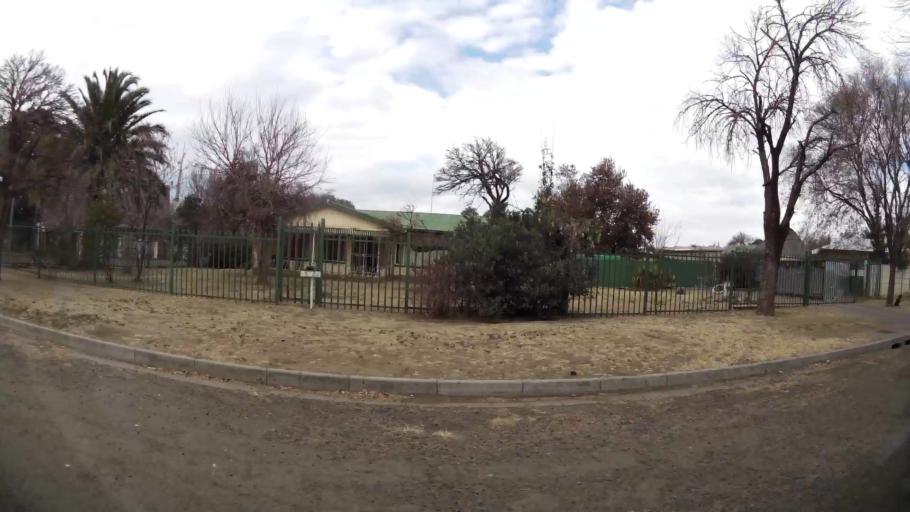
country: ZA
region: Orange Free State
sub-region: Fezile Dabi District Municipality
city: Kroonstad
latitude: -27.6508
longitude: 27.2406
